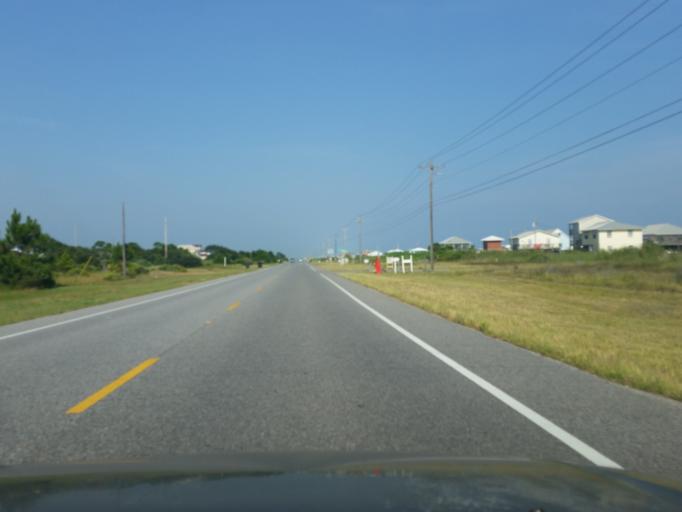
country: US
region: Alabama
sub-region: Mobile County
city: Dauphin Island
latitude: 30.2313
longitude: -87.9885
